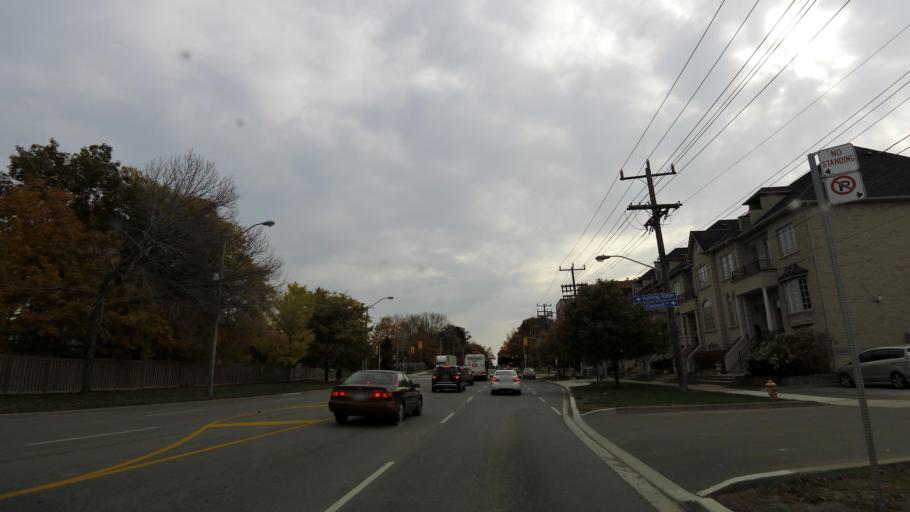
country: CA
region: Ontario
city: Etobicoke
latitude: 43.6820
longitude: -79.5532
